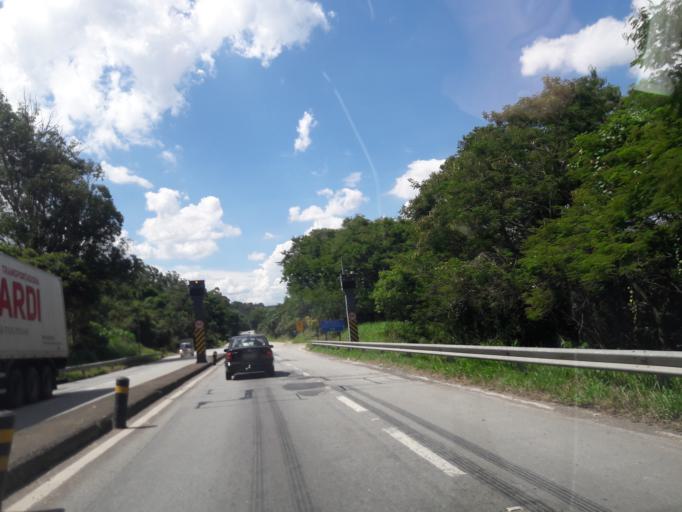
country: BR
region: Sao Paulo
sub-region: Francisco Morato
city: Francisco Morato
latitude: -23.3036
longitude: -46.8110
